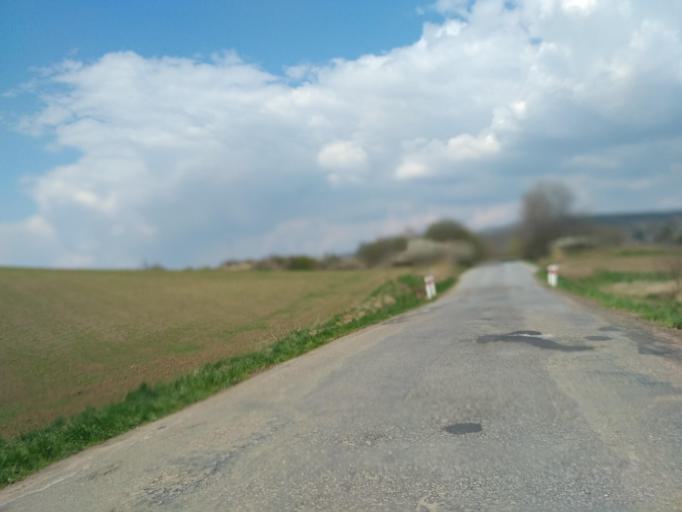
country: PL
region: Subcarpathian Voivodeship
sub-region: Powiat sanocki
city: Nowosielce-Gniewosz
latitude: 49.5509
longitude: 22.1071
